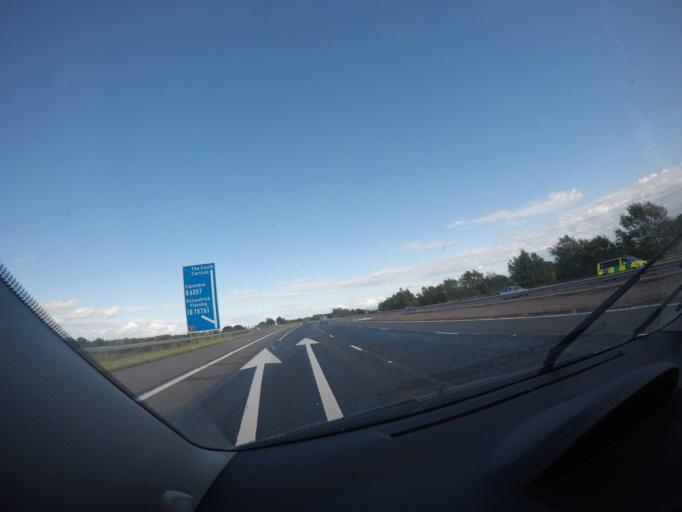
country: GB
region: Scotland
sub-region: Dumfries and Galloway
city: Gretna
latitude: 55.0279
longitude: -3.1356
